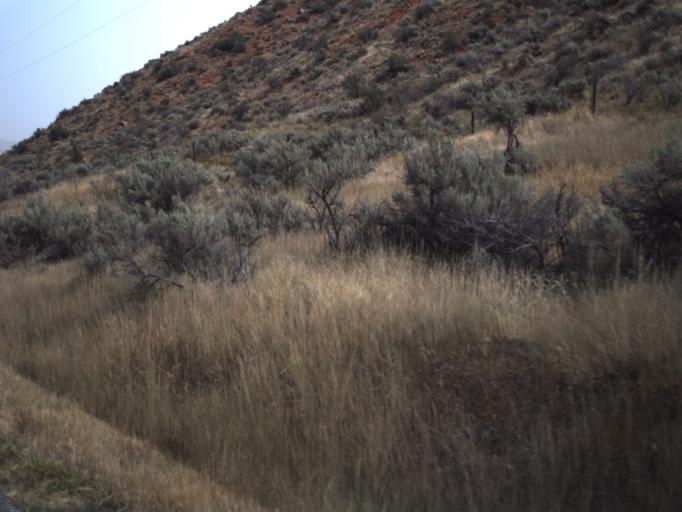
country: US
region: Utah
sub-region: Summit County
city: Coalville
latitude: 41.0102
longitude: -111.5167
